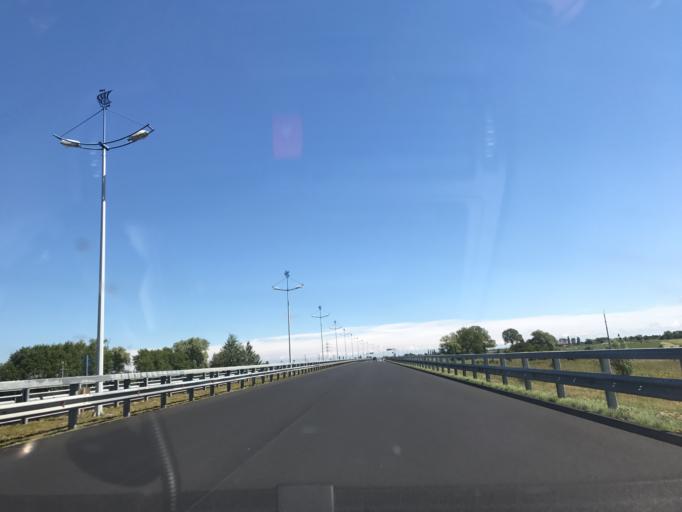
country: RU
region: Kaliningrad
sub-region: Zelenogradskiy Rayon
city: Zelenogradsk
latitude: 54.9197
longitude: 20.4452
